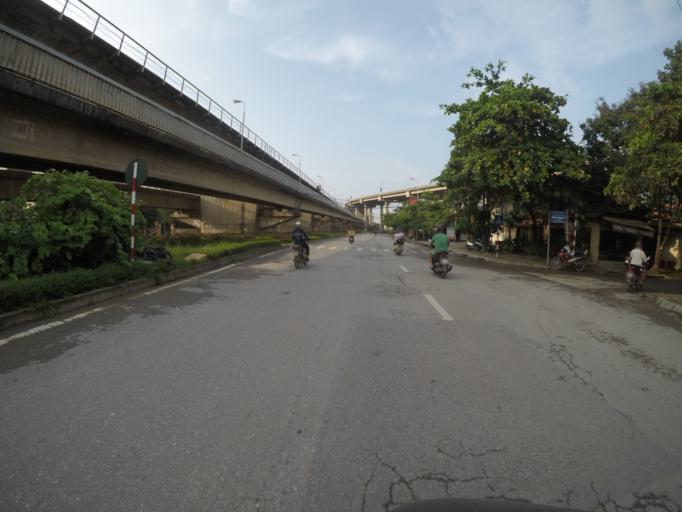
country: VN
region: Ha Noi
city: Tay Ho
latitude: 21.0875
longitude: 105.7858
